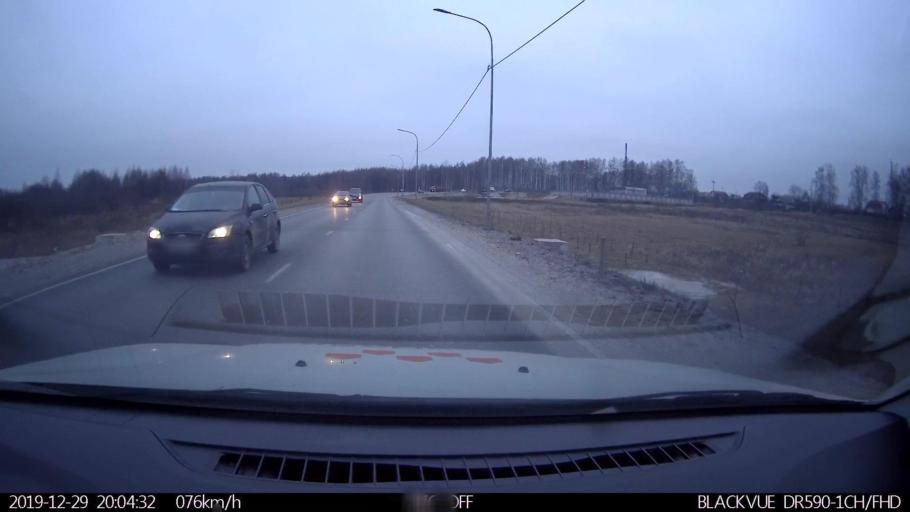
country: RU
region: Nizjnij Novgorod
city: Neklyudovo
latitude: 56.3850
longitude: 44.0095
